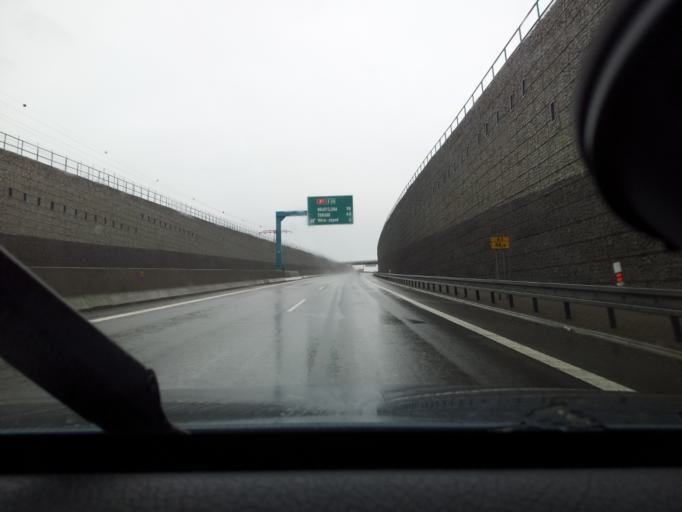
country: SK
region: Nitriansky
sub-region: Okres Nitra
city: Nitra
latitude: 48.2867
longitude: 18.0566
